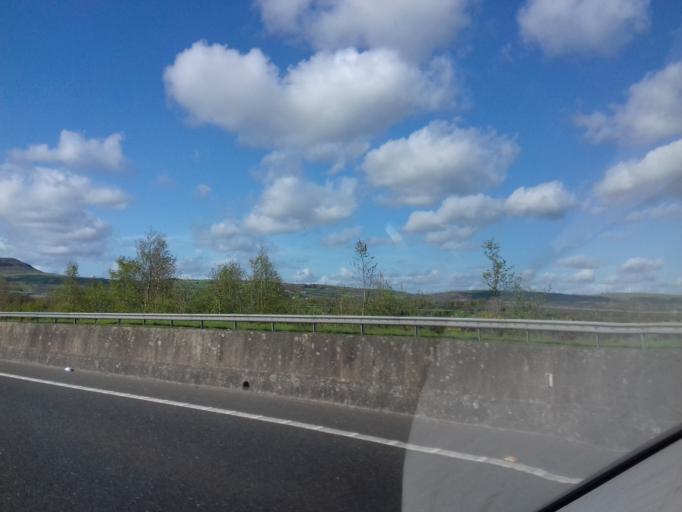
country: IE
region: Munster
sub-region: Waterford
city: Waterford
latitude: 52.3136
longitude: -7.1412
